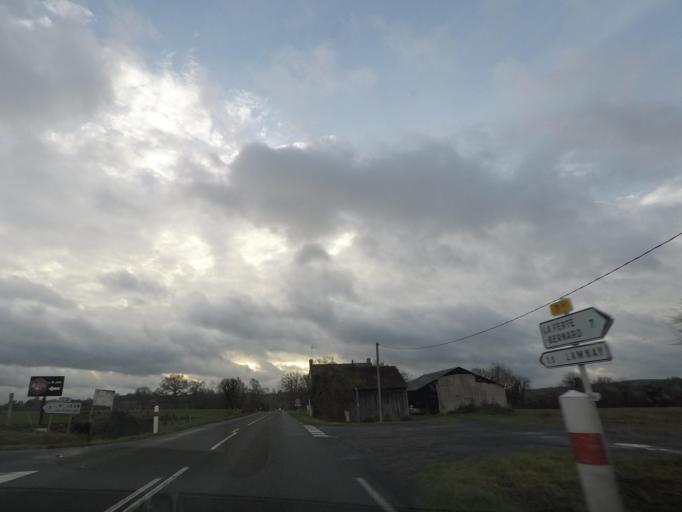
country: FR
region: Pays de la Loire
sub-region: Departement de la Sarthe
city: Cherre
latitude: 48.1297
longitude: 0.7003
